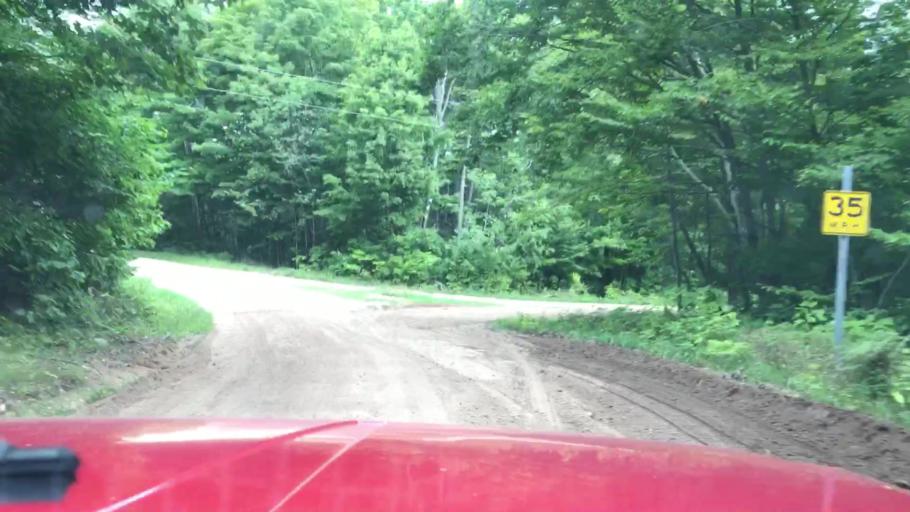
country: US
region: Michigan
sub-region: Charlevoix County
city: Charlevoix
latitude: 45.7261
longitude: -85.5647
